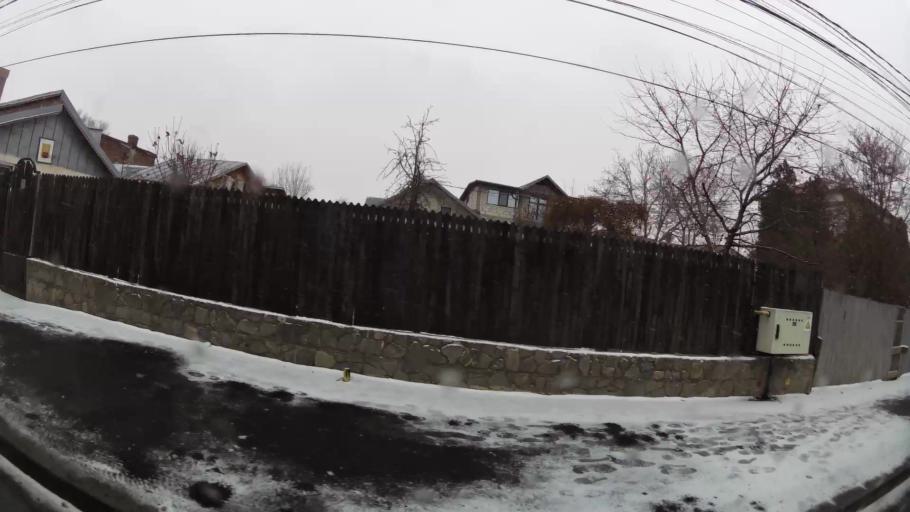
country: RO
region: Dambovita
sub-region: Municipiul Targoviste
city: Targoviste
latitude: 44.9289
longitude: 25.4693
